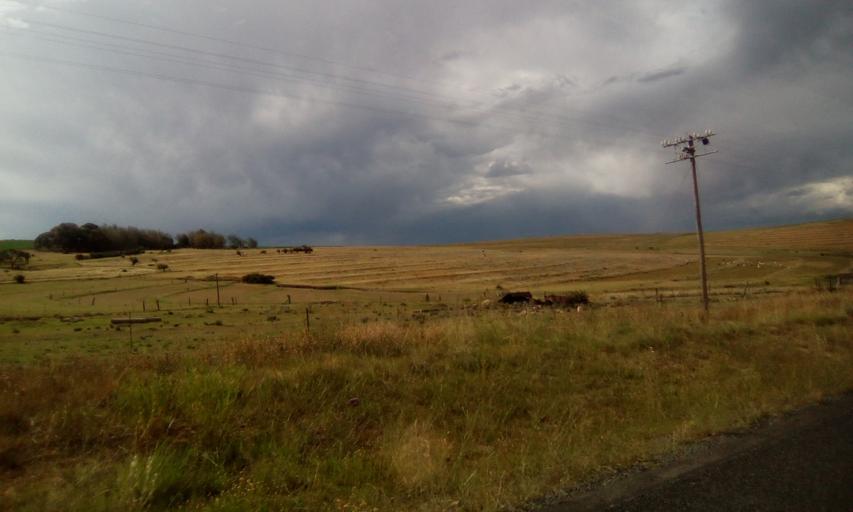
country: ZA
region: Orange Free State
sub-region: Thabo Mofutsanyana District Municipality
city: Ladybrand
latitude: -29.2325
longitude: 27.4500
